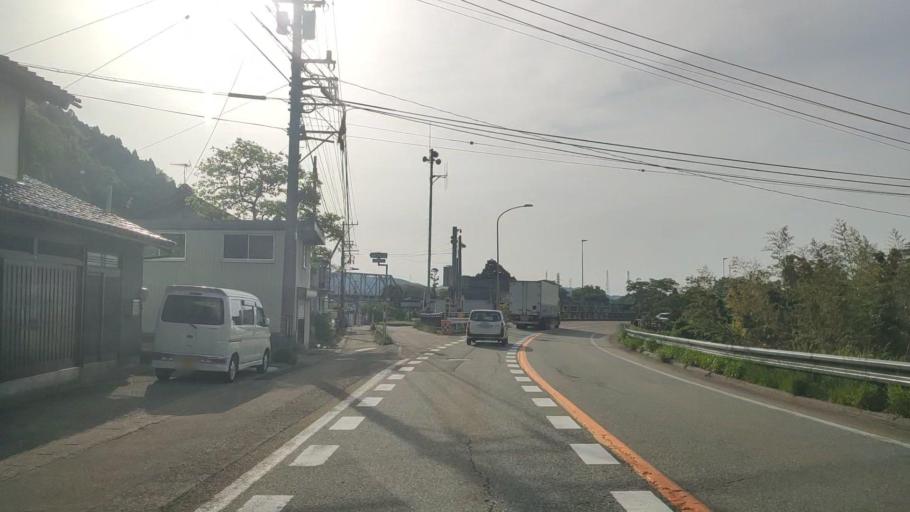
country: JP
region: Toyama
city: Yatsuomachi-higashikumisaka
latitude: 36.5566
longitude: 137.2166
